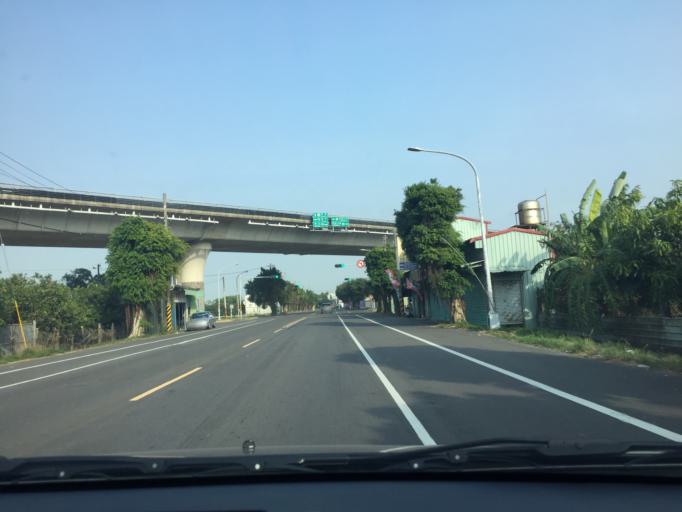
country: TW
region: Taiwan
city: Xinying
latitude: 23.1895
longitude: 120.2746
